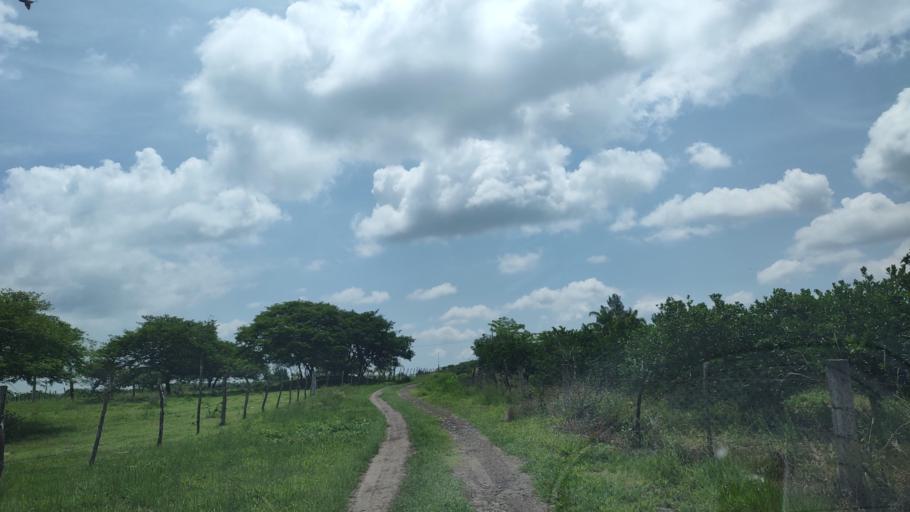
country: MX
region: Veracruz
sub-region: Emiliano Zapata
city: Dos Rios
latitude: 19.4662
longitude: -96.7976
